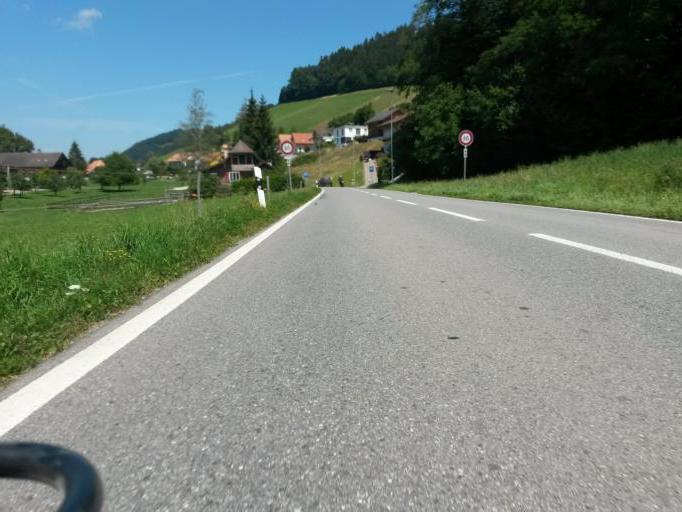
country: CH
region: Bern
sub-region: Bern-Mittelland District
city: Walkringen
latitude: 46.9389
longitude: 7.6159
